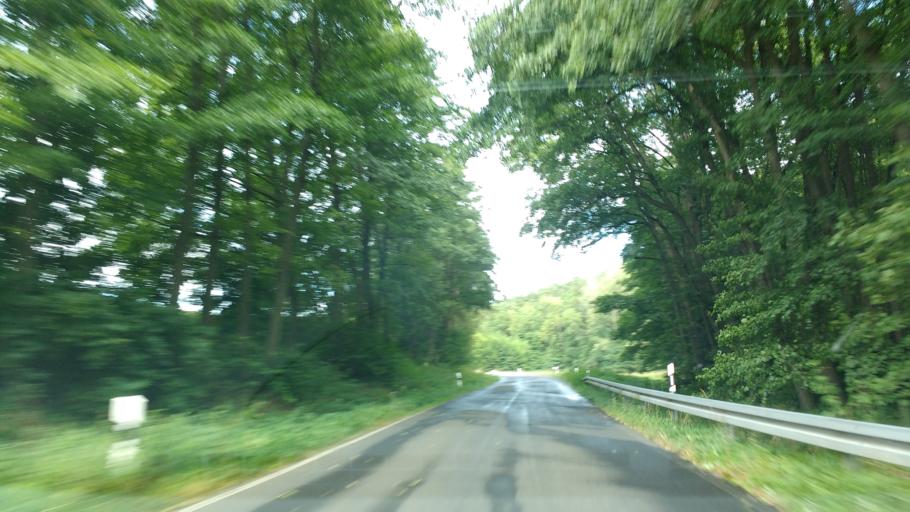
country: DE
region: Bavaria
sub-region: Regierungsbezirk Unterfranken
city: Geiselwind
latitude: 49.7855
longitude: 10.5219
